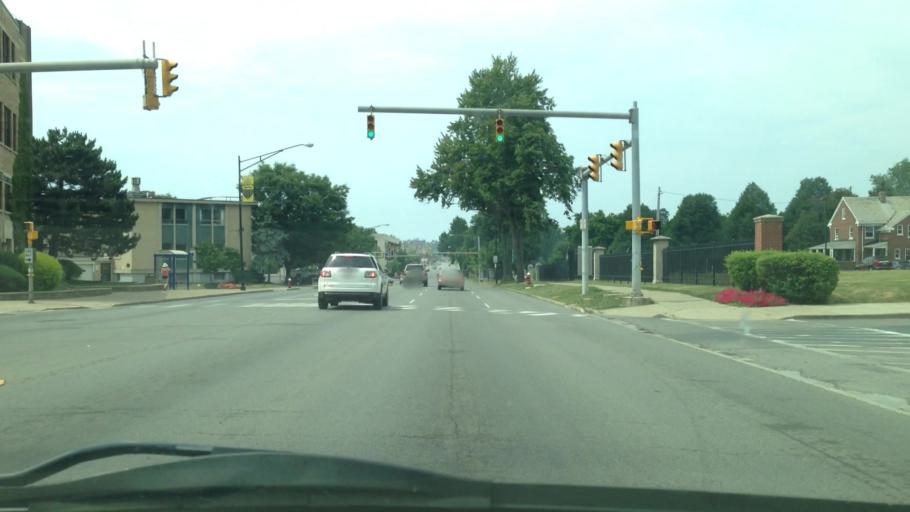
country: US
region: New York
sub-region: Erie County
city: Kenmore
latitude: 42.9266
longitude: -78.8527
